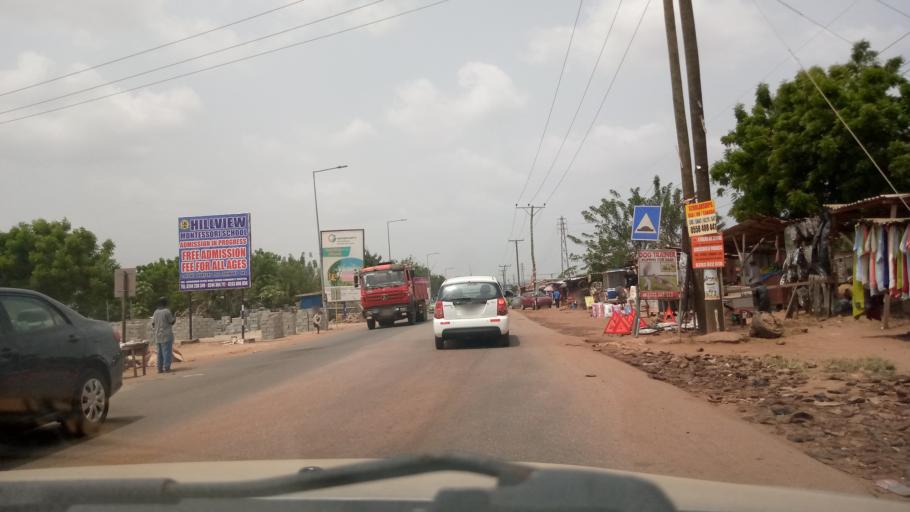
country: GH
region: Greater Accra
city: Dome
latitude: 5.6677
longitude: -0.2350
